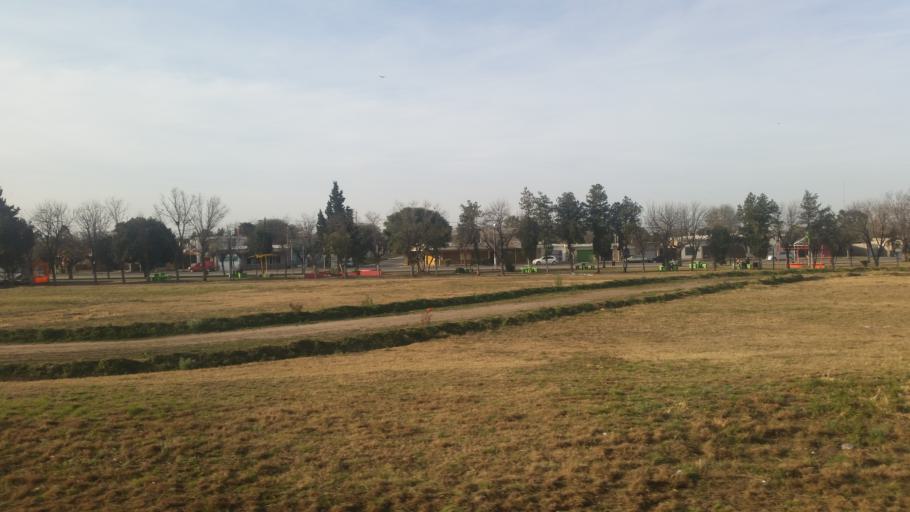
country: AR
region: Cordoba
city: Toledo
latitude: -31.5552
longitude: -64.0104
